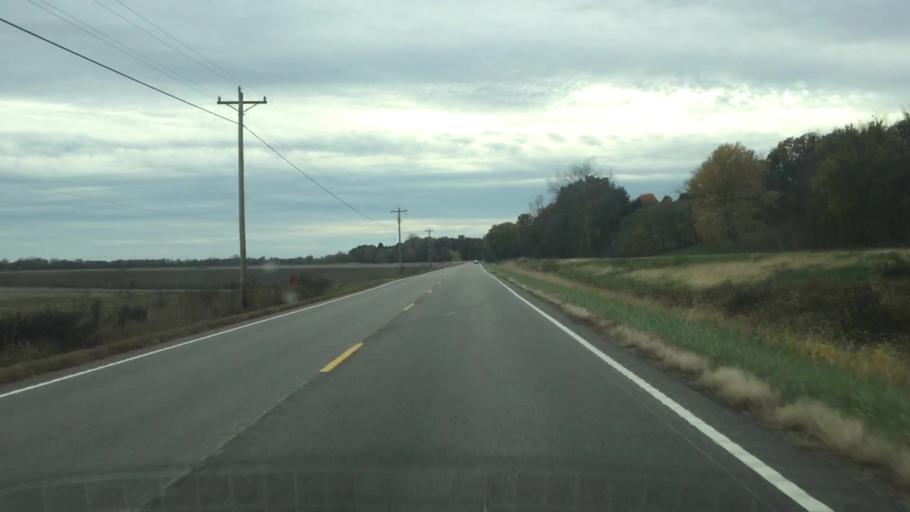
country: US
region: Missouri
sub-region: Callaway County
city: Fulton
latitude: 38.6898
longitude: -91.8449
